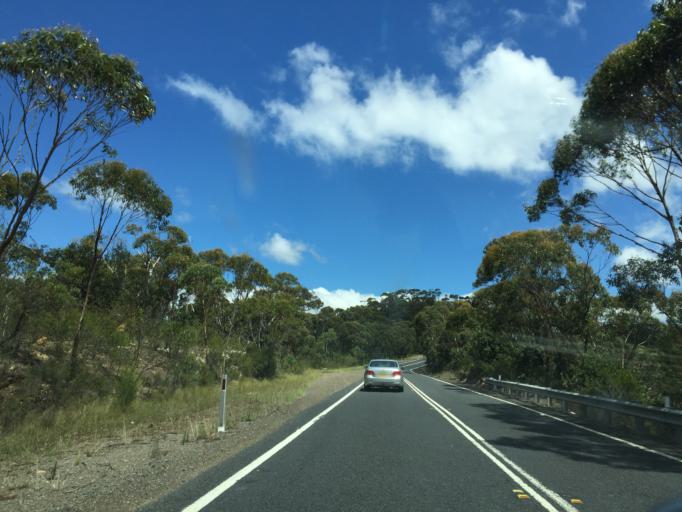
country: AU
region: New South Wales
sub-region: Blue Mountains Municipality
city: Blackheath
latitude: -33.5580
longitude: 150.3742
